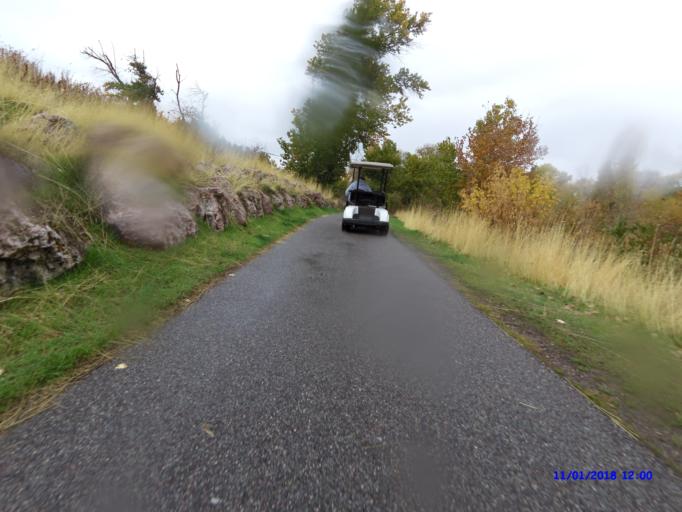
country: US
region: Utah
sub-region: Weber County
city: Ogden
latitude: 41.2326
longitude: -112.0013
